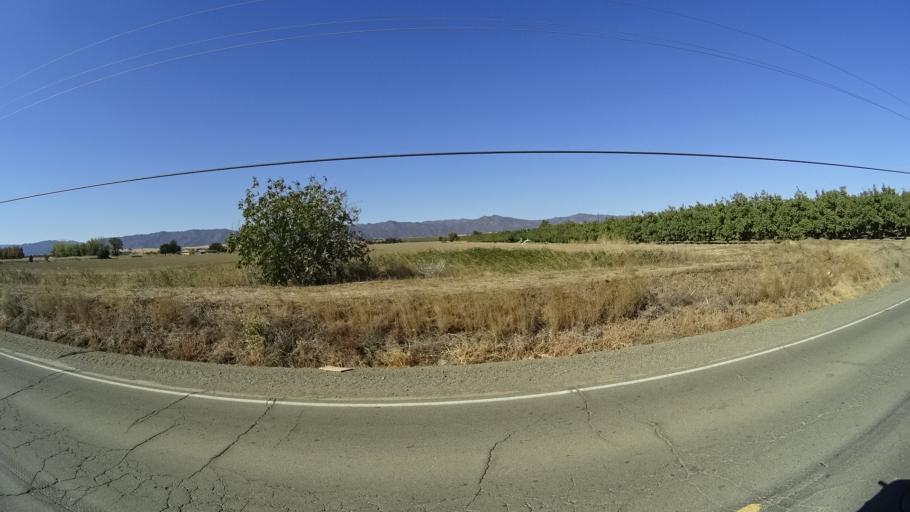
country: US
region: California
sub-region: Yolo County
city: Cottonwood
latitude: 38.6009
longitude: -121.9713
